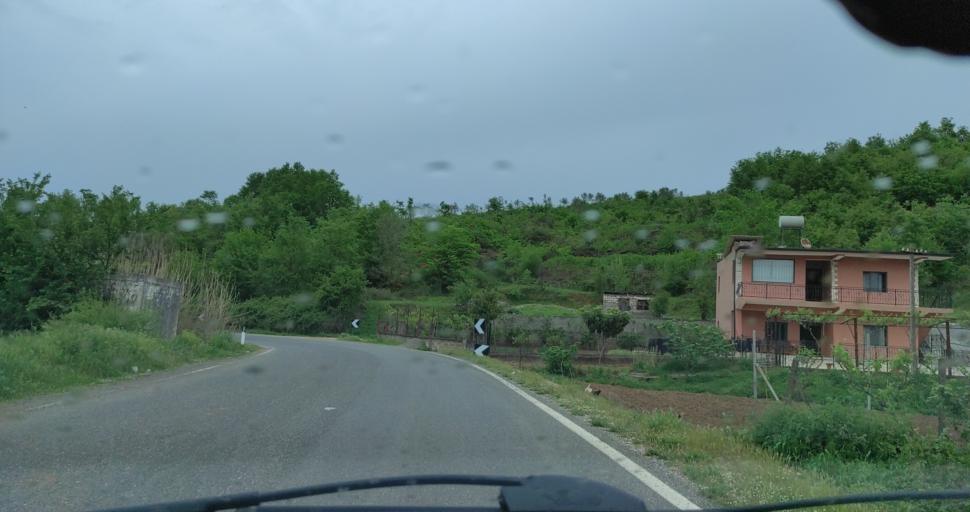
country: AL
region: Lezhe
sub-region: Rrethi i Kurbinit
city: Mamurras
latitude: 41.5898
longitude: 19.7002
